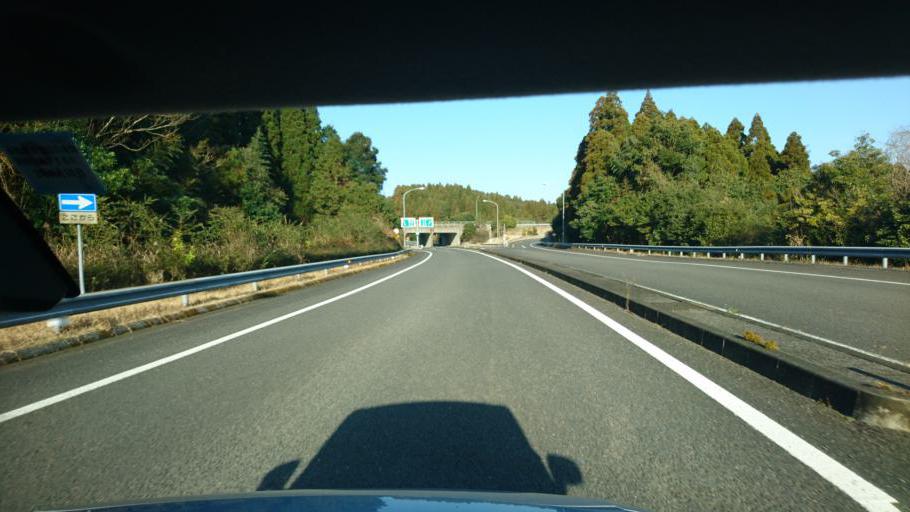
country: JP
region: Miyazaki
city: Miyazaki-shi
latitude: 31.8678
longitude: 131.3610
